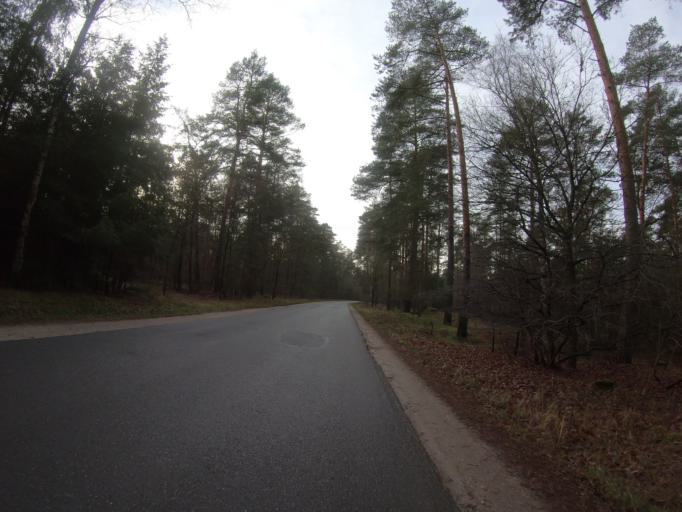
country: DE
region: Lower Saxony
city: Meinersen
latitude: 52.4905
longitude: 10.3950
